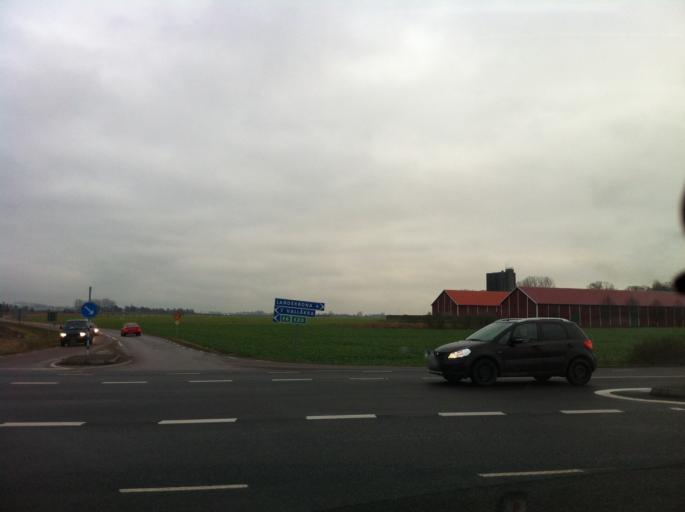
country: SE
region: Skane
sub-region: Landskrona
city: Landskrona
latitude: 55.9070
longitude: 12.8230
